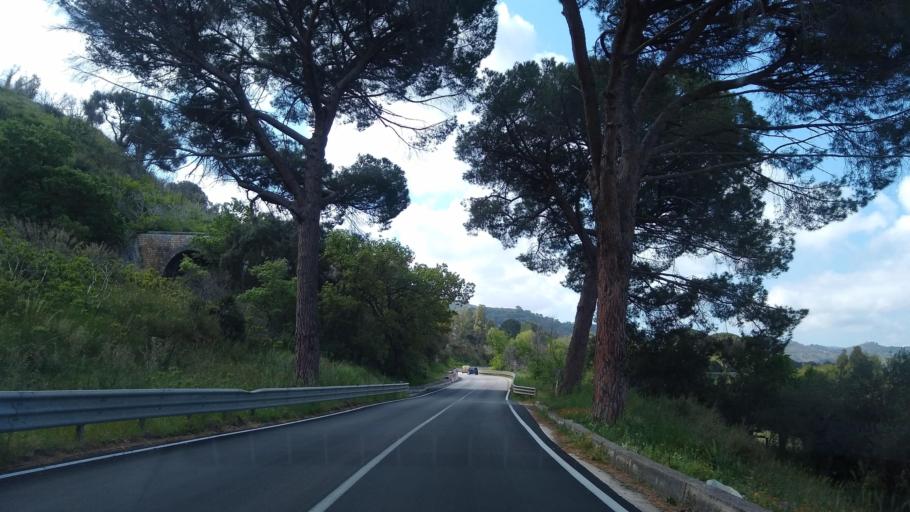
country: IT
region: Sicily
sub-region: Trapani
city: Calatafimi
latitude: 37.9474
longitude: 12.8615
